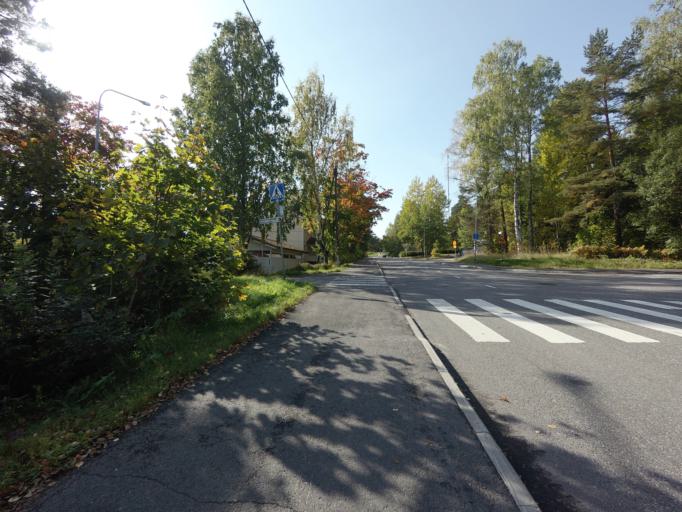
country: FI
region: Uusimaa
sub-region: Helsinki
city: Espoo
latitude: 60.1791
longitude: 24.6563
